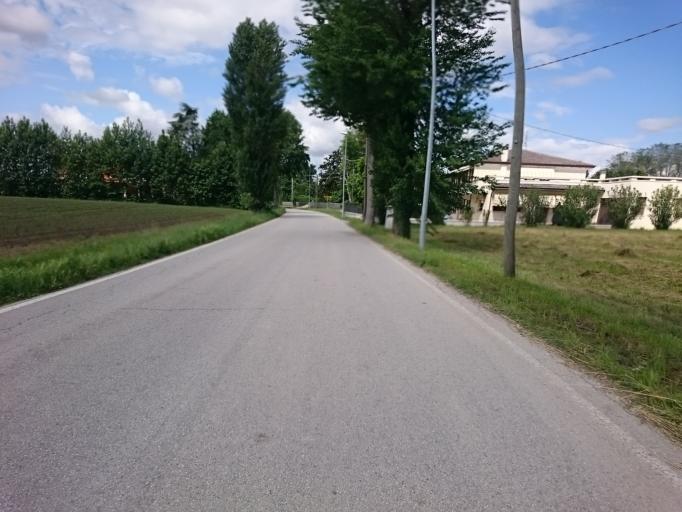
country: IT
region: Veneto
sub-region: Provincia di Padova
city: Arlesega
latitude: 45.4612
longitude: 11.7412
